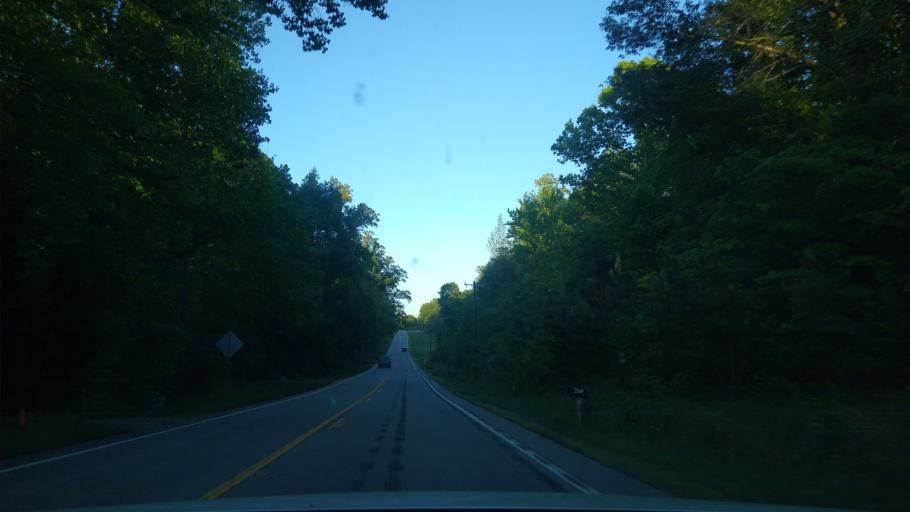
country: US
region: North Carolina
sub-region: Rockingham County
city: Reidsville
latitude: 36.3941
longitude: -79.5485
